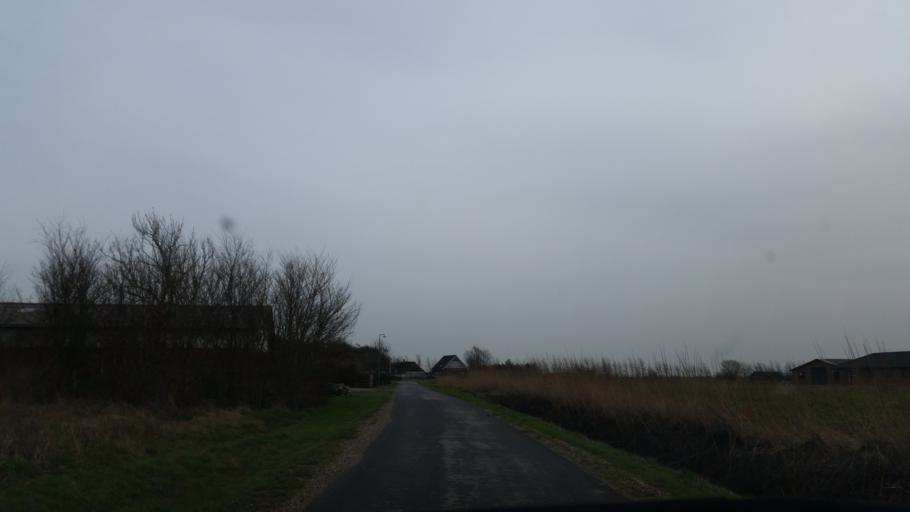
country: DE
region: Schleswig-Holstein
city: Klanxbull
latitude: 54.9838
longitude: 8.6710
